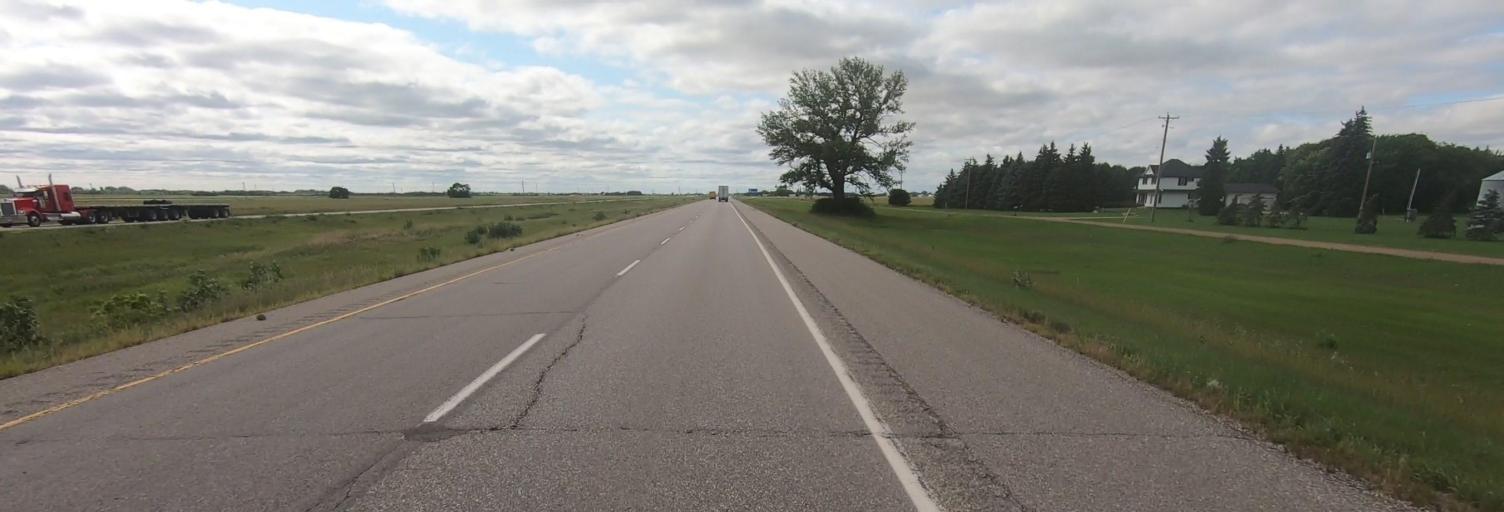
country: CA
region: Manitoba
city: Brandon
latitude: 49.8870
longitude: -99.8517
